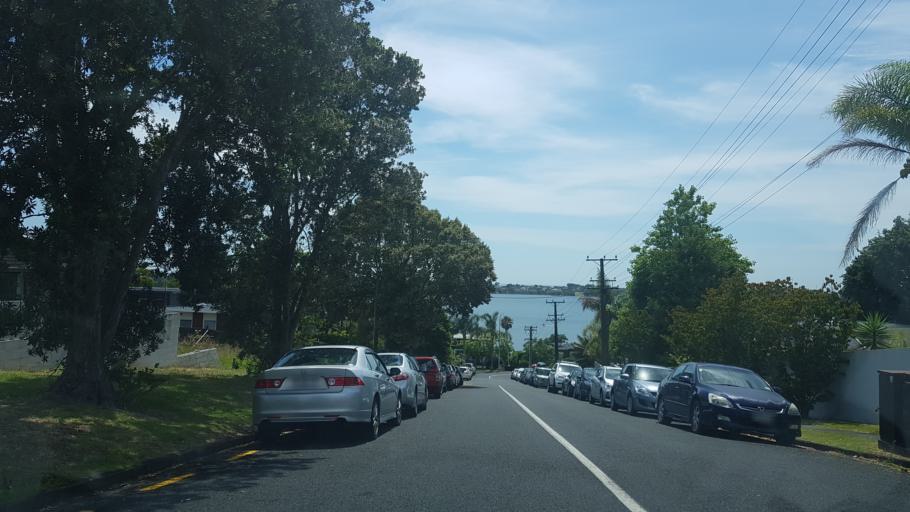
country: NZ
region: Auckland
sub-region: Auckland
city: North Shore
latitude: -36.7853
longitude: 174.7597
